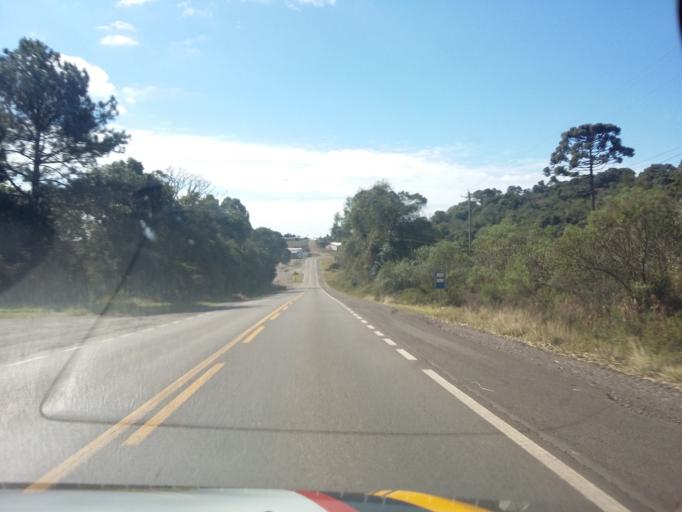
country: BR
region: Rio Grande do Sul
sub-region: Sao Marcos
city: Sao Marcos
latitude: -28.7838
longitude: -51.0986
